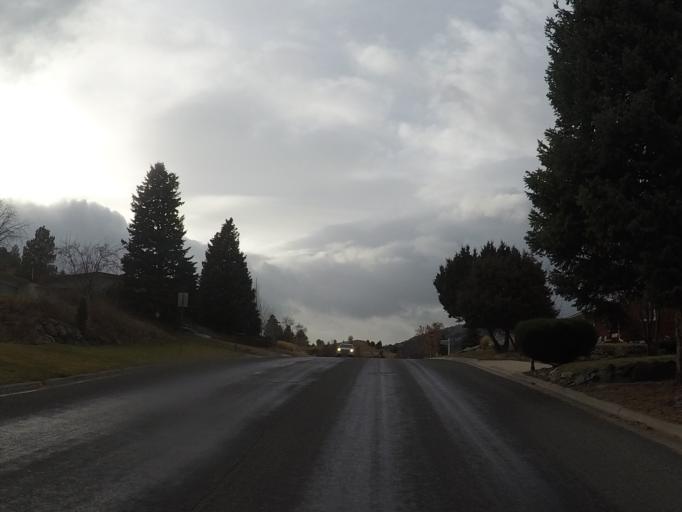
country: US
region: Montana
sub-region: Lewis and Clark County
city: Helena
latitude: 46.5813
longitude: -112.0152
